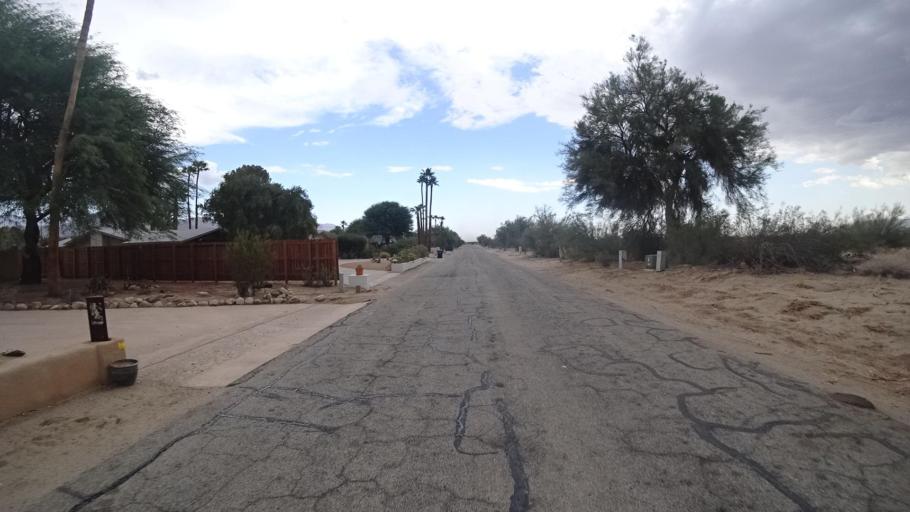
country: US
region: California
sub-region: San Diego County
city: Borrego Springs
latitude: 33.2875
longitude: -116.3839
